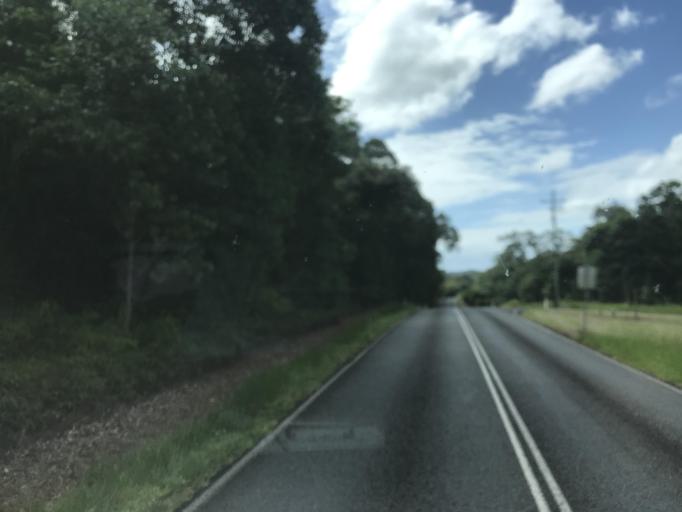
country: AU
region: Queensland
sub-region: Cassowary Coast
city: Innisfail
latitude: -17.8409
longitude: 146.0539
